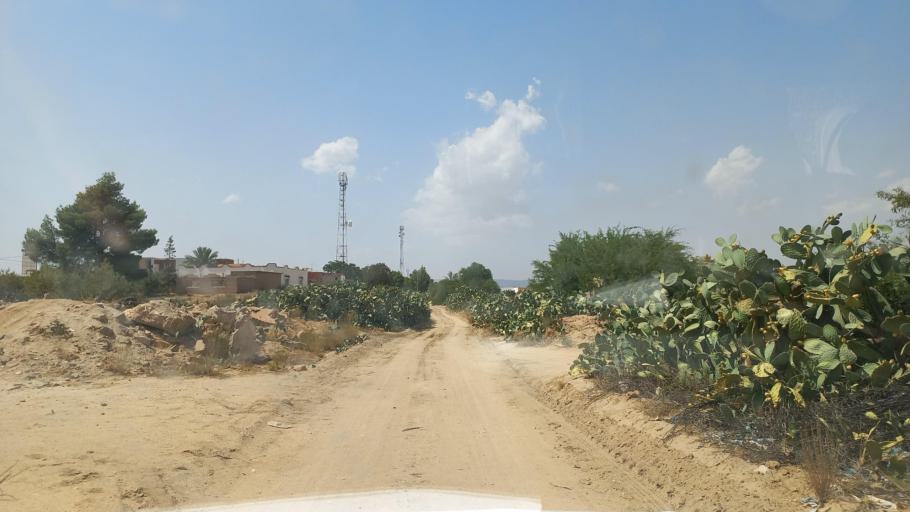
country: TN
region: Al Qasrayn
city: Kasserine
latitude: 35.2518
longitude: 9.0288
